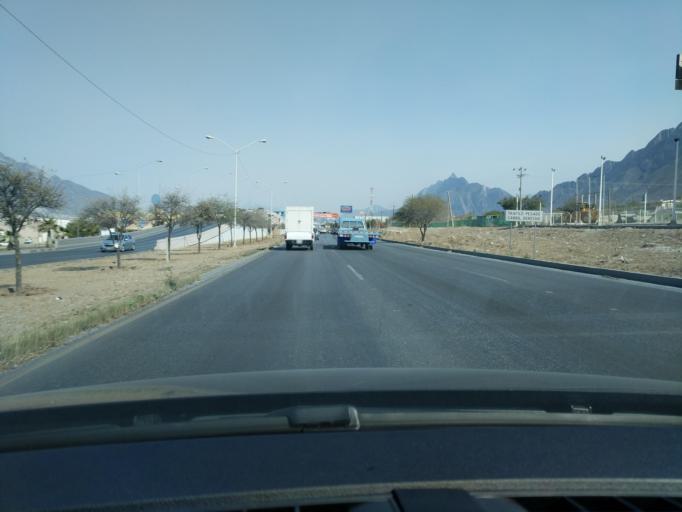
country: MX
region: Nuevo Leon
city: Santa Catarina
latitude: 25.6888
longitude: -100.4992
